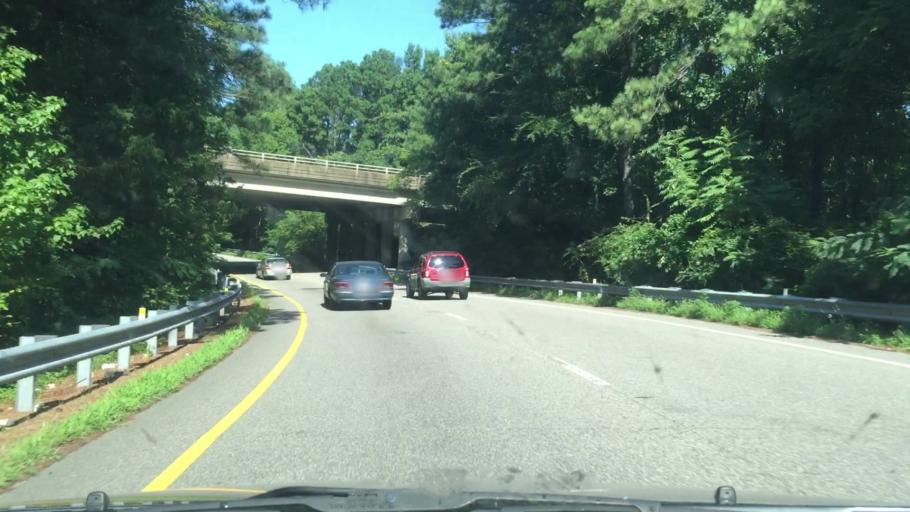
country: US
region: Virginia
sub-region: Henrico County
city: Dumbarton
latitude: 37.5990
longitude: -77.4904
